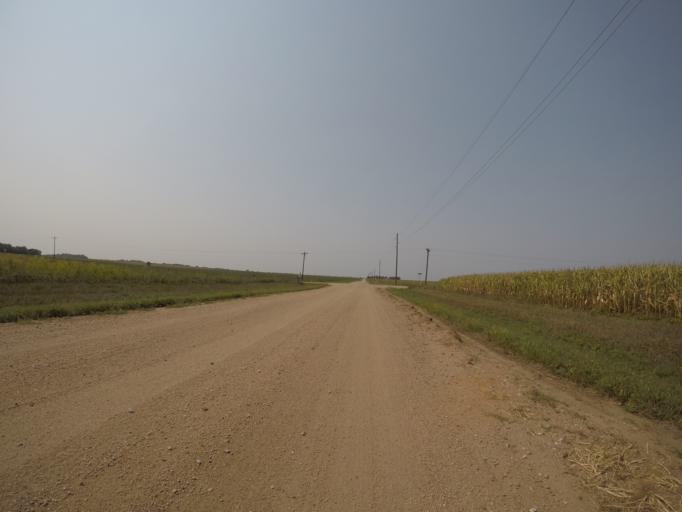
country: US
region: Nebraska
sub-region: Gage County
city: Beatrice
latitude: 40.2774
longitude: -96.8215
